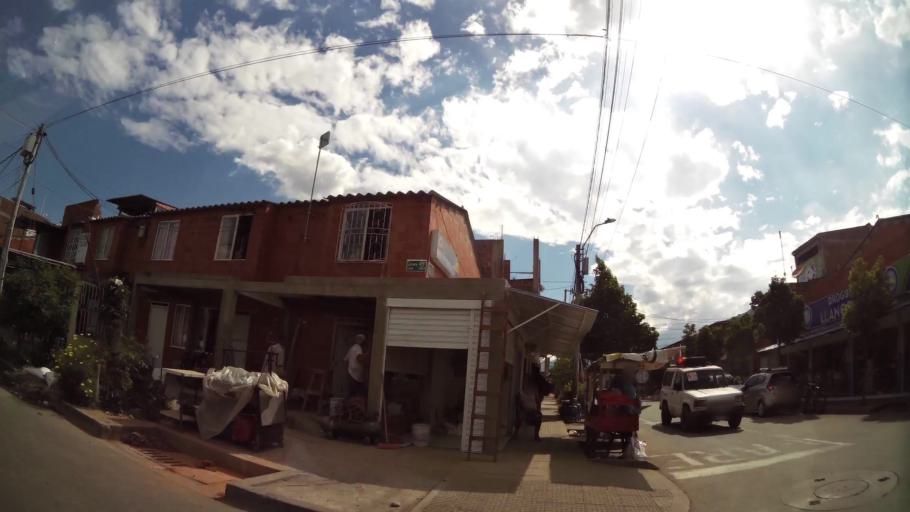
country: CO
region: Valle del Cauca
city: Cali
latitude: 3.3922
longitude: -76.5073
